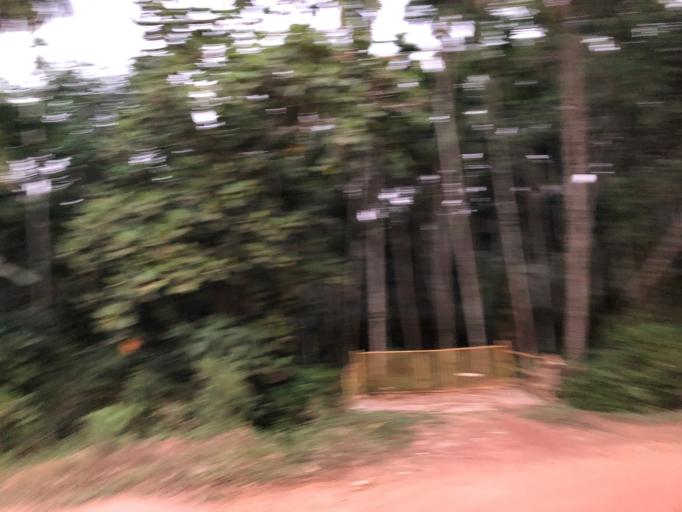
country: IN
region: Karnataka
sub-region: Dakshina Kannada
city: Mangalore
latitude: 12.8919
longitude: 74.8644
